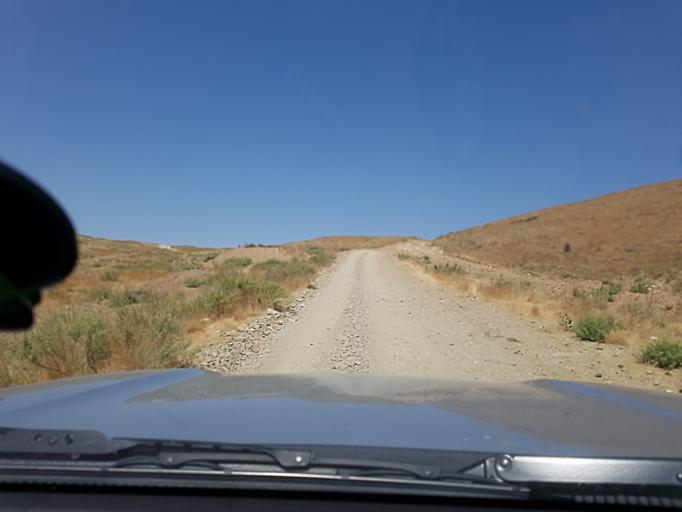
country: TM
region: Balkan
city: Magtymguly
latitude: 38.3526
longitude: 56.8407
